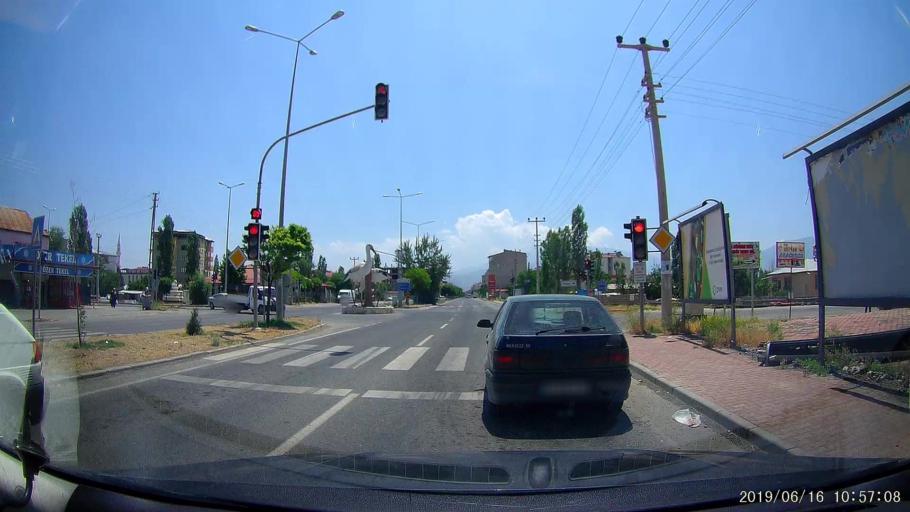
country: TR
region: Igdir
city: Igdir
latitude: 39.9277
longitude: 44.0260
